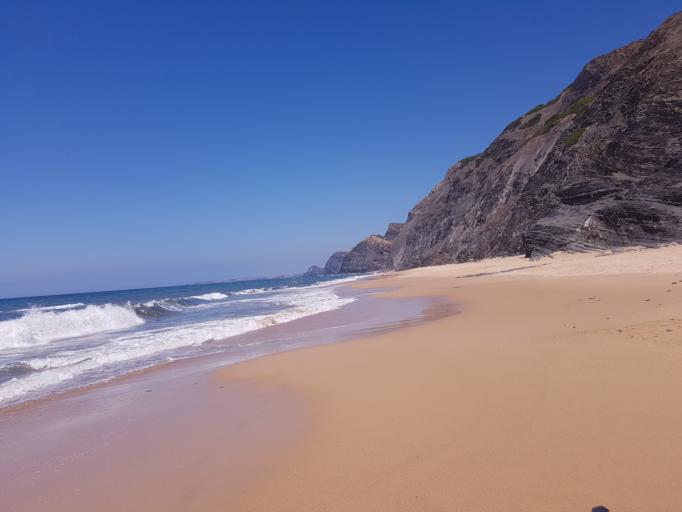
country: PT
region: Faro
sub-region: Vila do Bispo
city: Vila do Bispo
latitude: 37.1132
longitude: -8.9345
